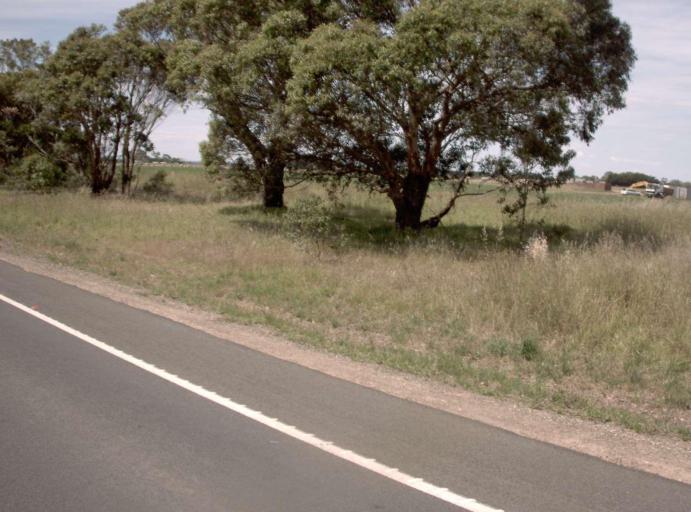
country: AU
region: Victoria
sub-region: Wellington
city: Sale
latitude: -38.0839
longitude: 147.0708
